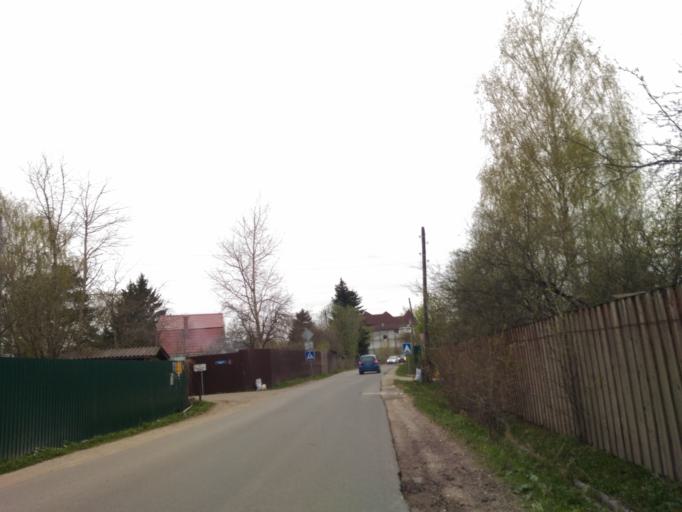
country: RU
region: Moskovskaya
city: Dedovsk
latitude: 55.8528
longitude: 37.1391
